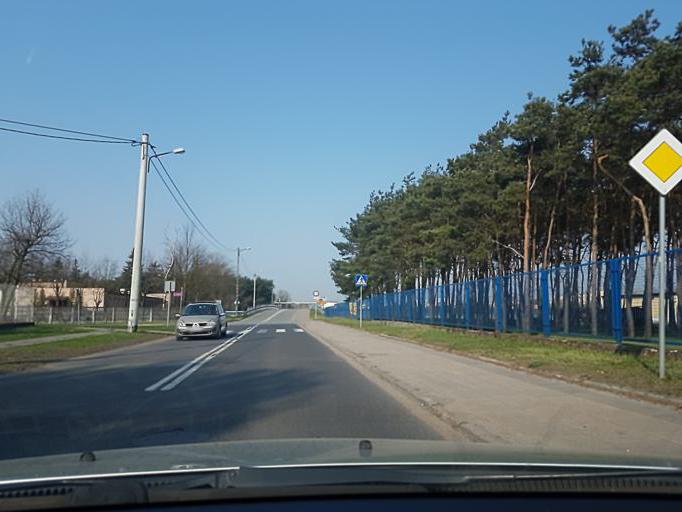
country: PL
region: Lodz Voivodeship
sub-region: Powiat kutnowski
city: Kutno
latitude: 52.2214
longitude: 19.3857
